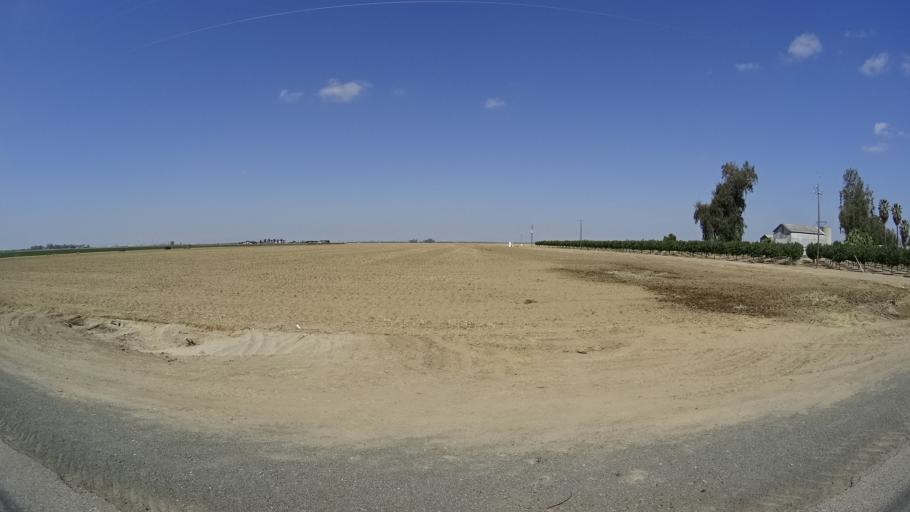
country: US
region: California
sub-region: Kings County
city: Home Garden
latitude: 36.2382
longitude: -119.6369
